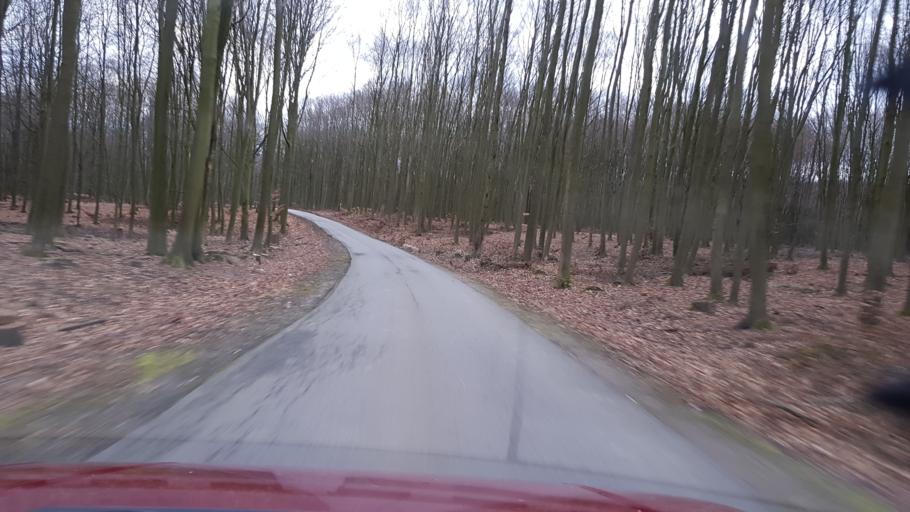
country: PL
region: West Pomeranian Voivodeship
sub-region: Powiat gryfinski
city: Stare Czarnowo
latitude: 53.3115
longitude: 14.7236
